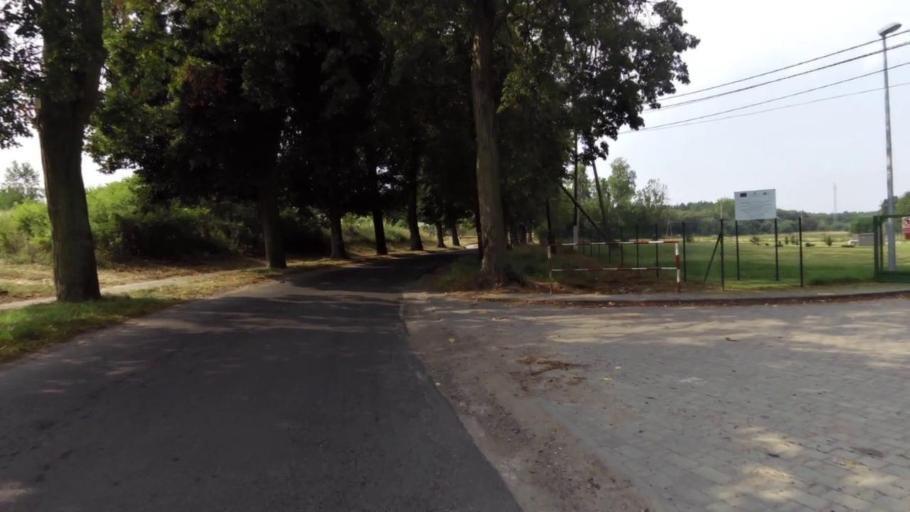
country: PL
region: West Pomeranian Voivodeship
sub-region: Powiat mysliborski
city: Mysliborz
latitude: 52.8476
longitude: 14.7796
